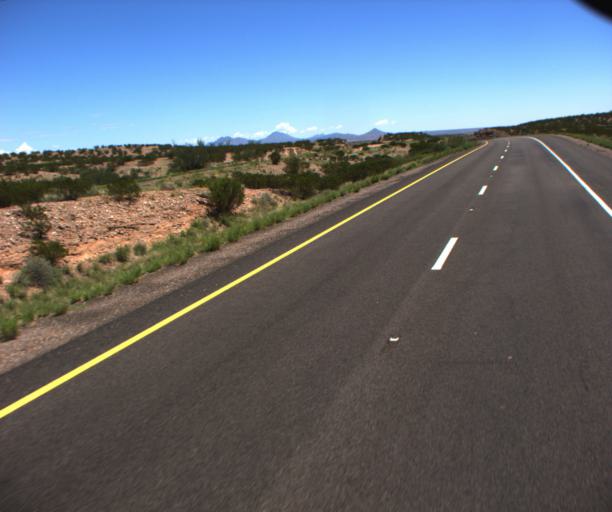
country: US
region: Arizona
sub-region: Greenlee County
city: Clifton
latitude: 32.9856
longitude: -109.2646
